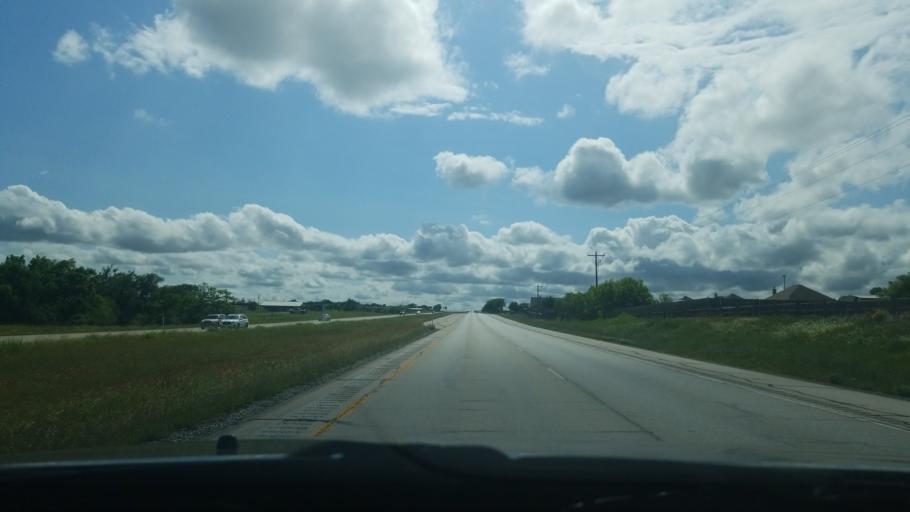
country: US
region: Texas
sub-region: Denton County
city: Ponder
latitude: 33.2508
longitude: -97.4163
